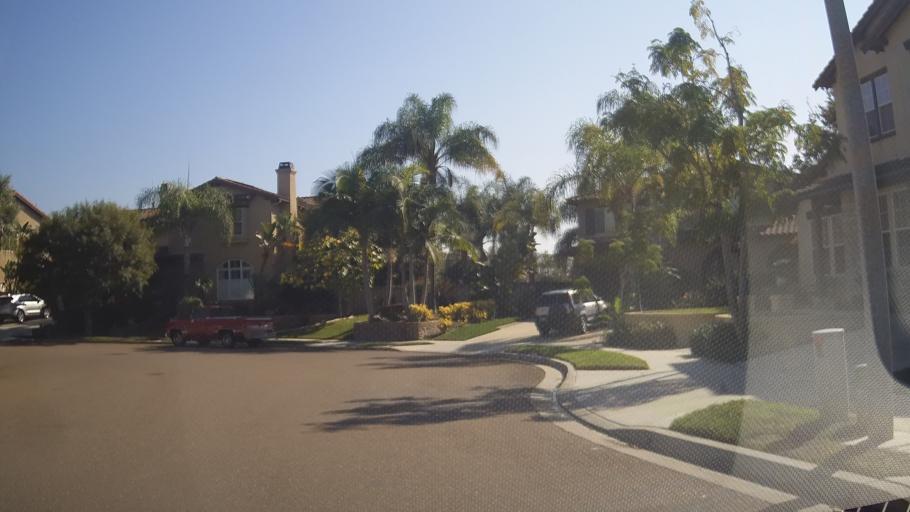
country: US
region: California
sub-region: San Diego County
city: Fairbanks Ranch
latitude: 33.0073
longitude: -117.1206
